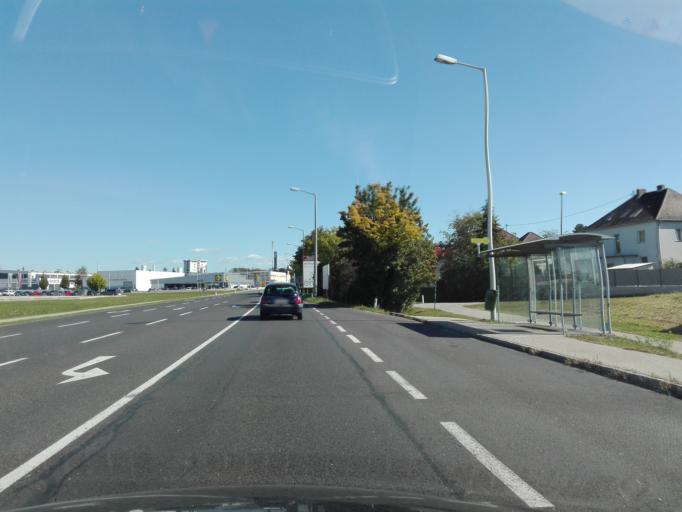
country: AT
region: Upper Austria
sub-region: Politischer Bezirk Linz-Land
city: Enns
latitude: 48.2158
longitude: 14.4659
